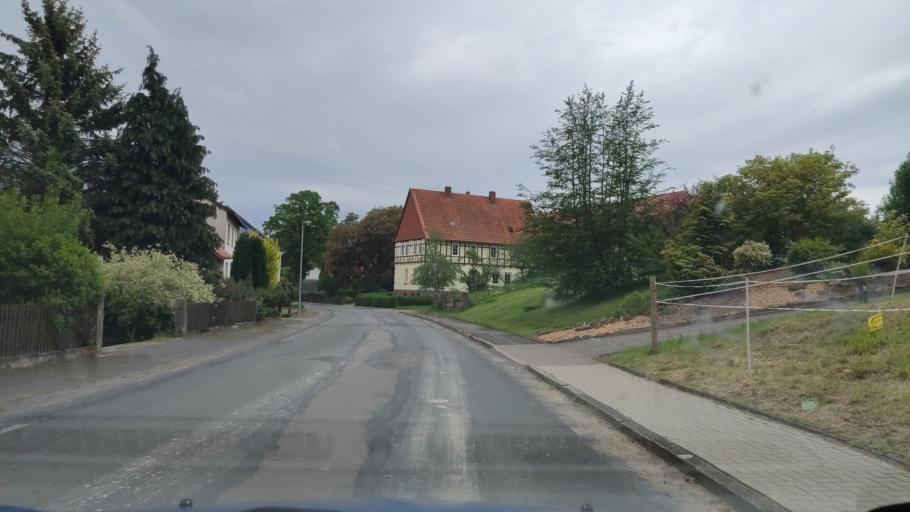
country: DE
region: Lower Saxony
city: Hardegsen
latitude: 51.6855
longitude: 9.8079
